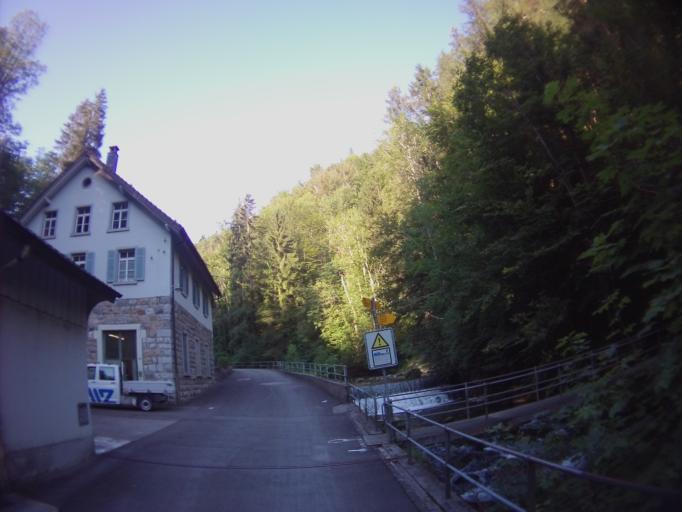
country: CH
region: Zug
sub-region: Zug
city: Menzingen
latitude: 47.1685
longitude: 8.5599
